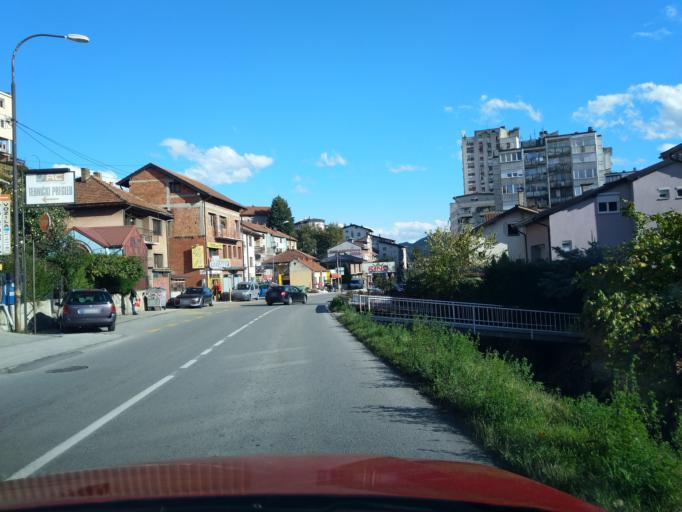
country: RS
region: Central Serbia
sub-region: Zlatiborski Okrug
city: Uzice
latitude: 43.8578
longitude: 19.8325
